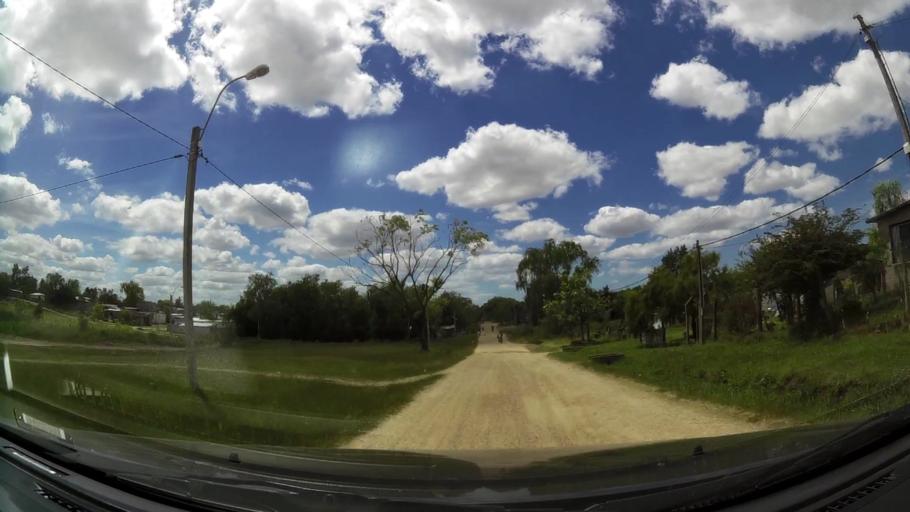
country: UY
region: Canelones
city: Colonia Nicolich
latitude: -34.7915
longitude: -55.9972
